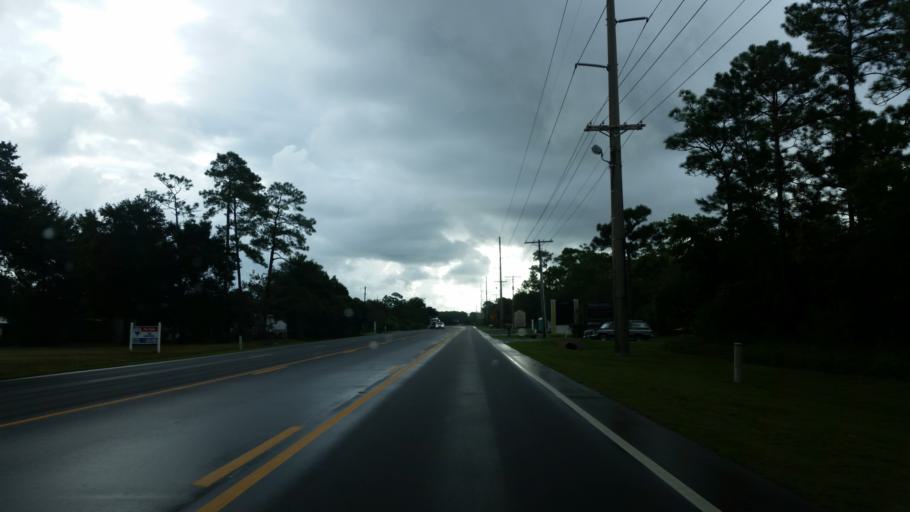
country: US
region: Alabama
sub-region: Baldwin County
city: Orange Beach
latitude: 30.2903
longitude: -87.5916
